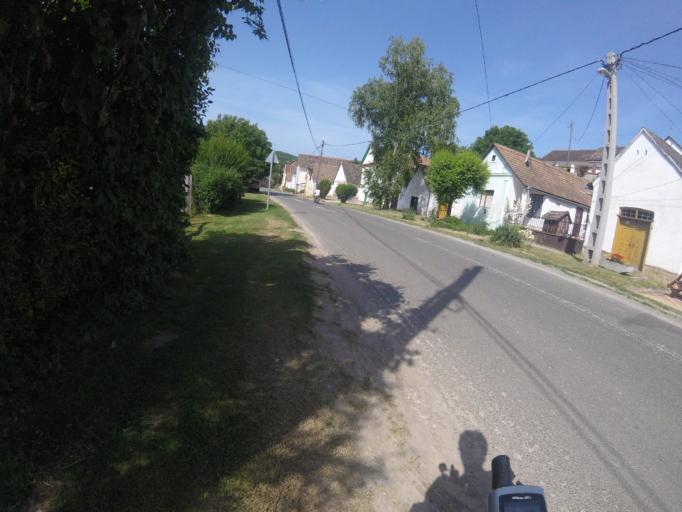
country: HU
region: Baranya
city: Villany
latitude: 45.8810
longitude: 18.4280
